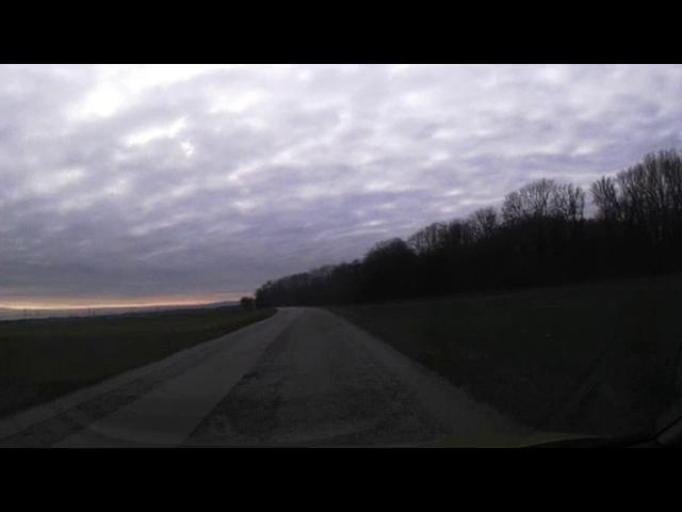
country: AT
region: Lower Austria
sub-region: Politischer Bezirk Wiener Neustadt
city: Ebenfurth
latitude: 47.8965
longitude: 16.3516
